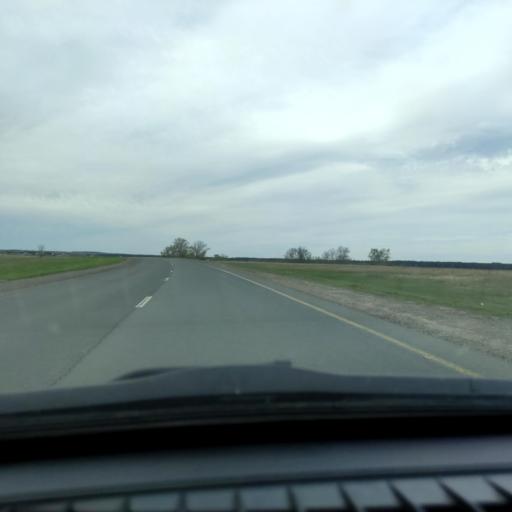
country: RU
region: Samara
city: Krasnyy Yar
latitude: 53.5332
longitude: 50.3628
